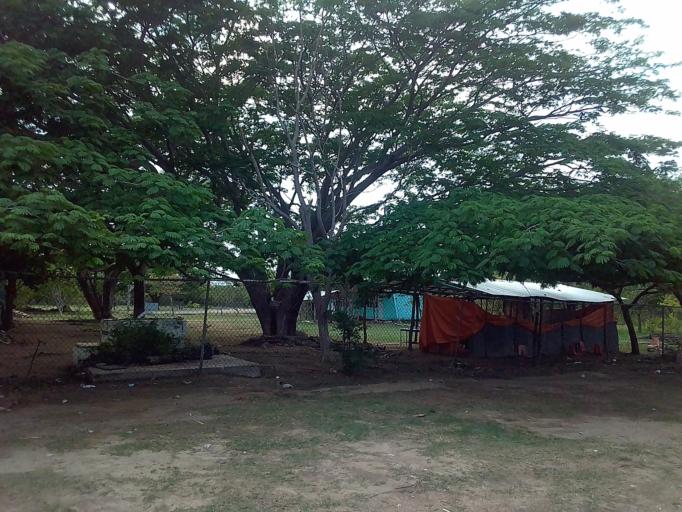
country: MX
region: Oaxaca
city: San Dionisio del Mar
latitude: 16.3297
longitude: -94.7578
